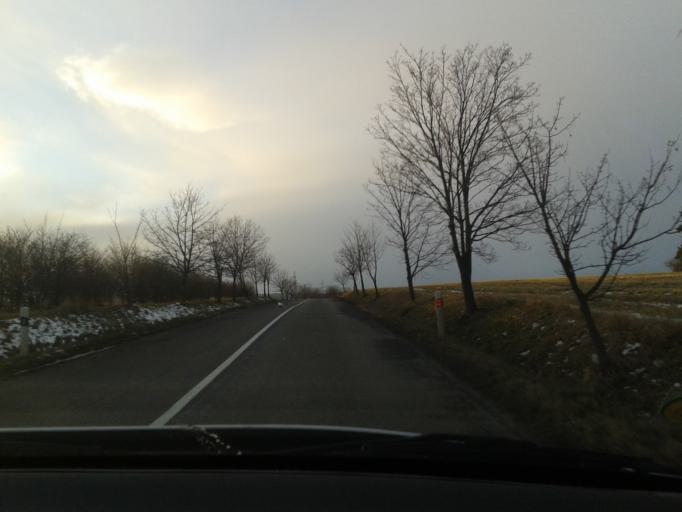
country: CZ
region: Olomoucky
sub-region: Okres Prostejov
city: Plumlov
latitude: 49.4897
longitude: 17.0122
